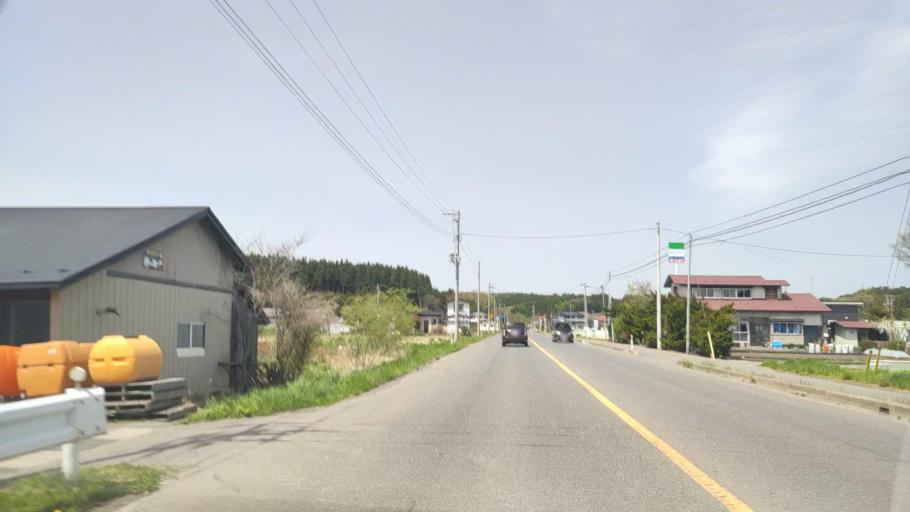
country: JP
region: Aomori
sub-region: Misawa Shi
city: Inuotose
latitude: 40.5586
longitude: 141.3867
